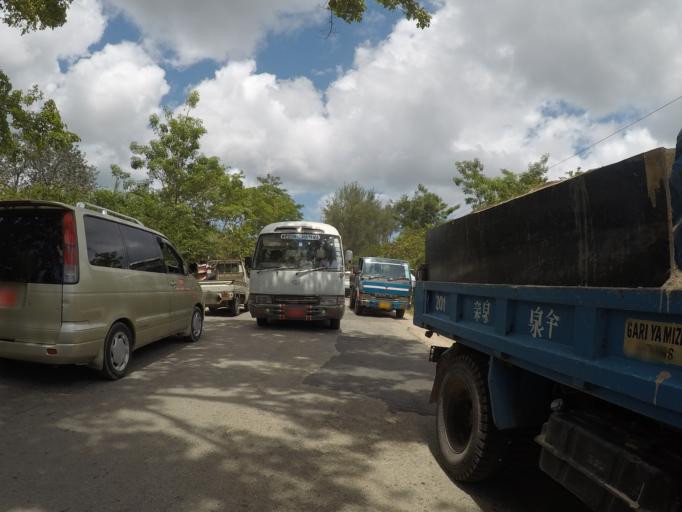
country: TZ
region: Zanzibar Central/South
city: Mahonda
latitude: -6.2747
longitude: 39.4174
